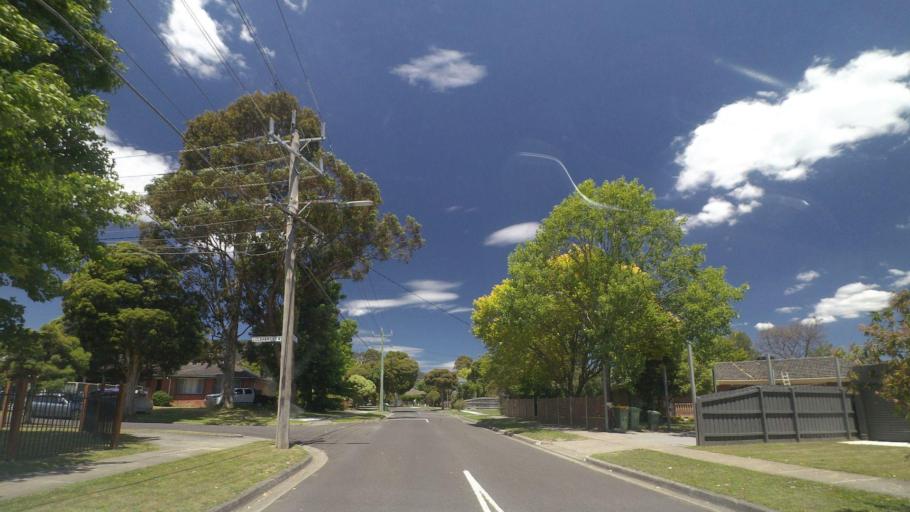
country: AU
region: Victoria
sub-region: Maroondah
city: Kilsyth South
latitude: -37.8104
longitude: 145.3209
